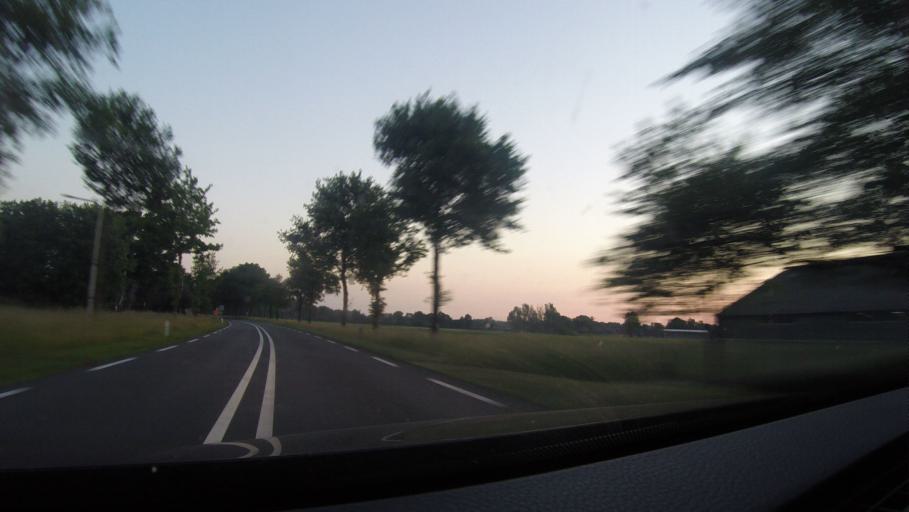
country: NL
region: Gelderland
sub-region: Gemeente Lochem
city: Laren
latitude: 52.1810
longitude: 6.3821
